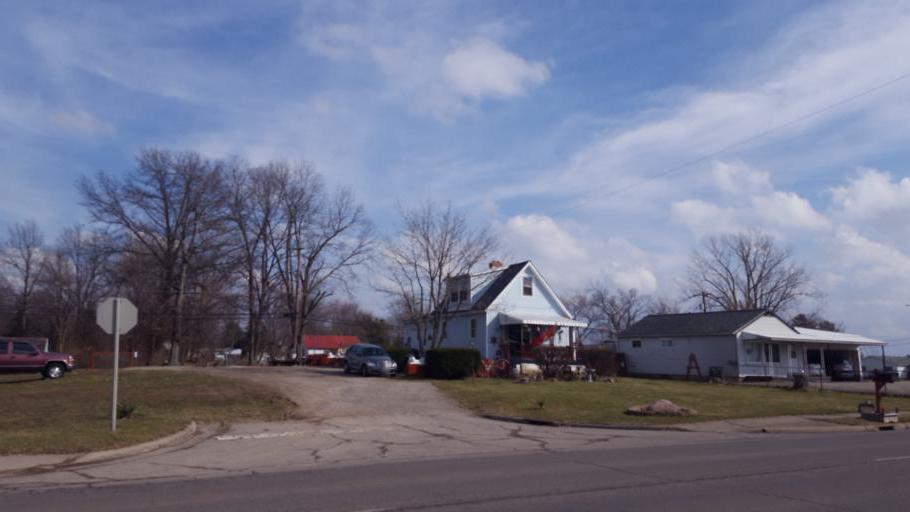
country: US
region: Ohio
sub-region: Richland County
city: Mansfield
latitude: 40.7787
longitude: -82.5519
